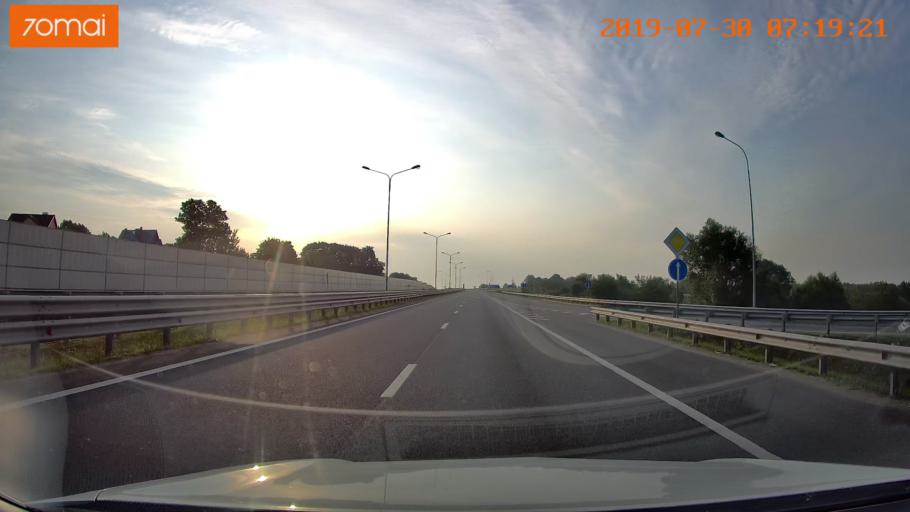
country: RU
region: Kaliningrad
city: Bol'shoe Isakovo
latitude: 54.7013
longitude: 20.6727
